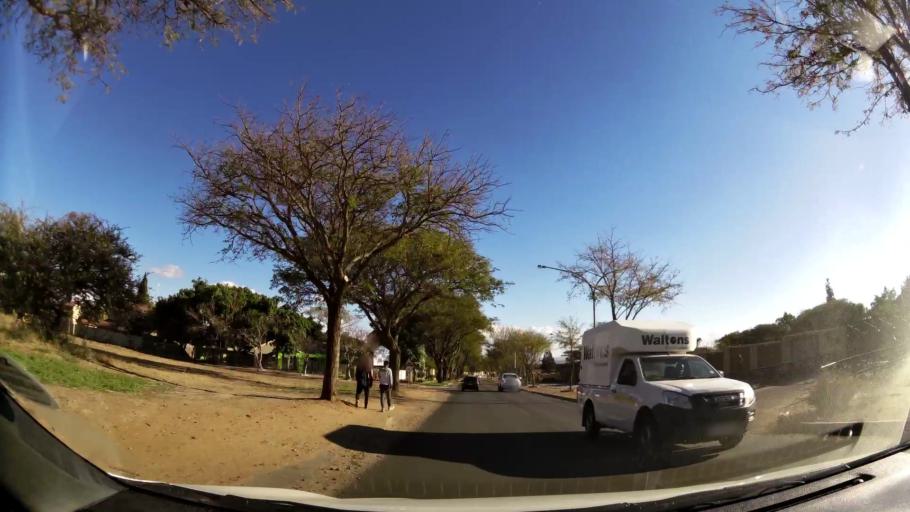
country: ZA
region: Limpopo
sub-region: Capricorn District Municipality
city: Polokwane
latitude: -23.8896
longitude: 29.4781
